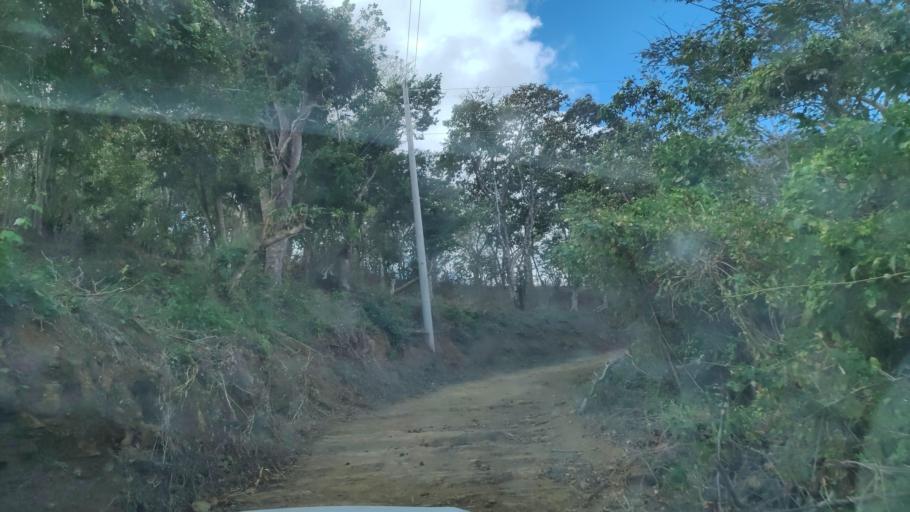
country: NI
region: Carazo
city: Santa Teresa
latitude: 11.6517
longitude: -86.2014
